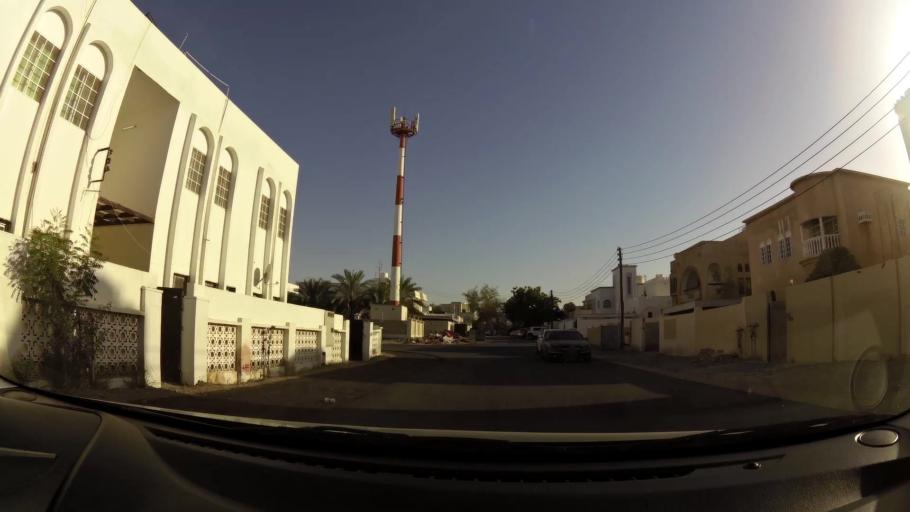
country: OM
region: Muhafazat Masqat
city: As Sib al Jadidah
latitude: 23.6325
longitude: 58.1958
